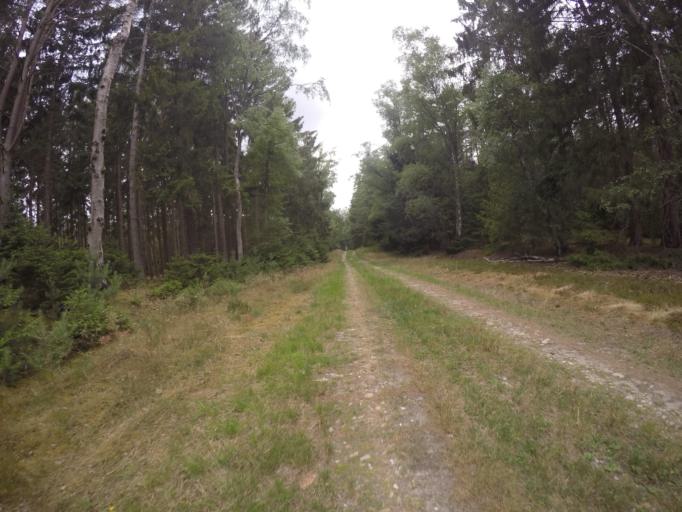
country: DE
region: Lower Saxony
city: Thomasburg
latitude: 53.2389
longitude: 10.6921
